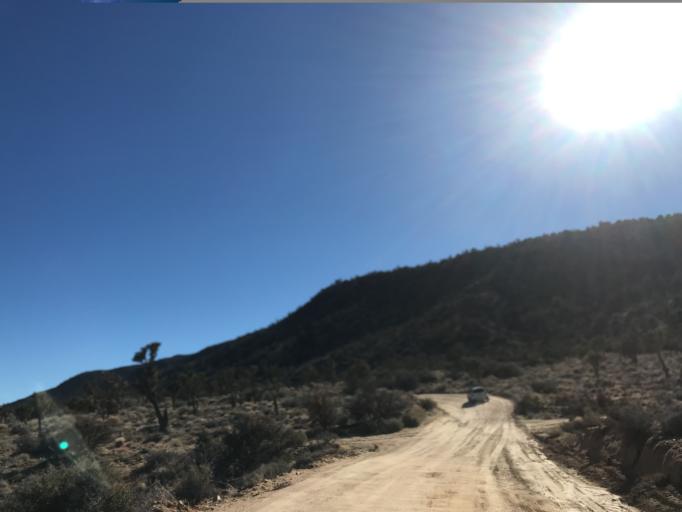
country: US
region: California
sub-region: San Bernardino County
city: Morongo Valley
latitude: 34.2218
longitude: -116.6215
